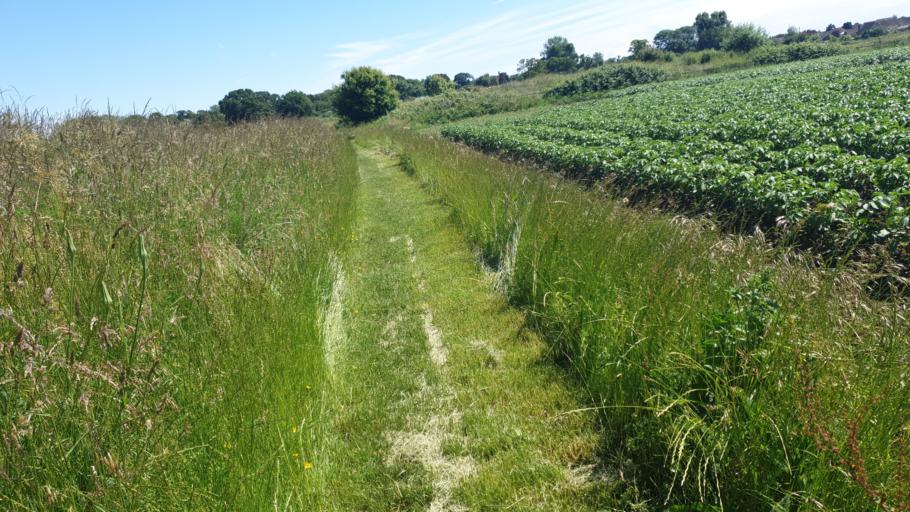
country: GB
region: England
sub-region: Essex
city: Saint Osyth
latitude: 51.7905
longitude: 1.1115
